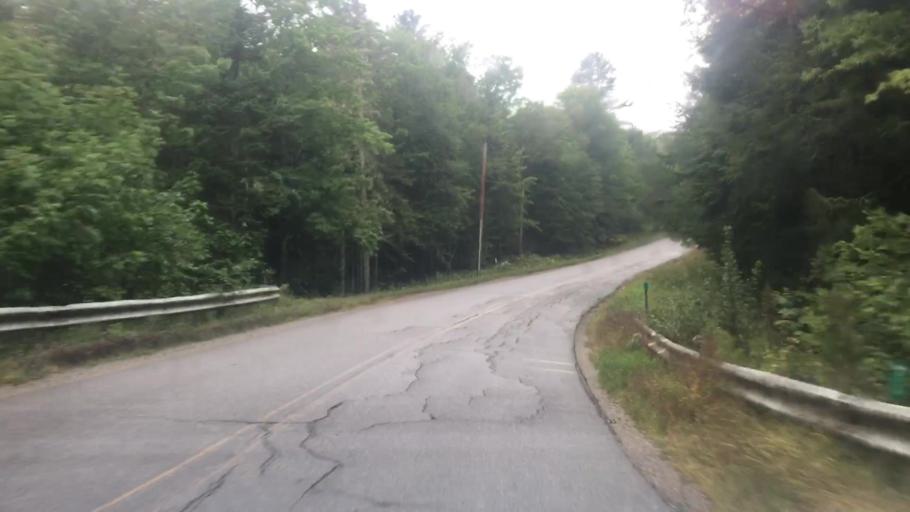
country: US
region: Maine
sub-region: Waldo County
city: Stockton Springs
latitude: 44.5407
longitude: -68.9066
